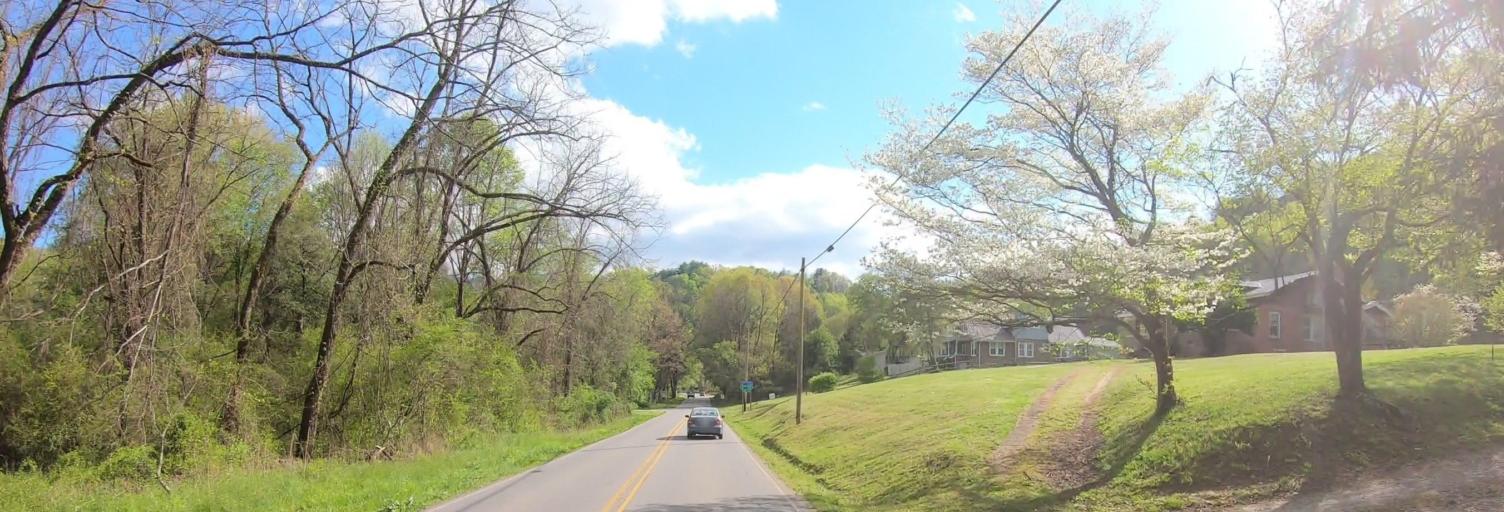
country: US
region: North Carolina
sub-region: Swain County
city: Bryson City
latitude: 35.4354
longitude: -83.4123
